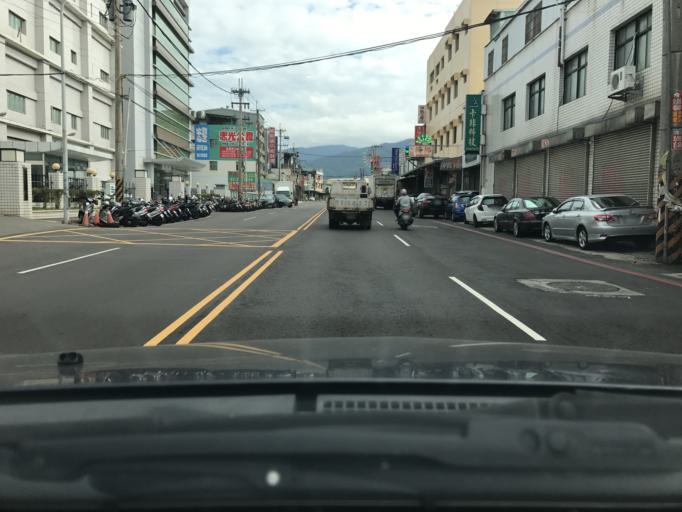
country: TW
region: Taiwan
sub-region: Hsinchu
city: Zhubei
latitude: 24.7338
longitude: 121.0984
